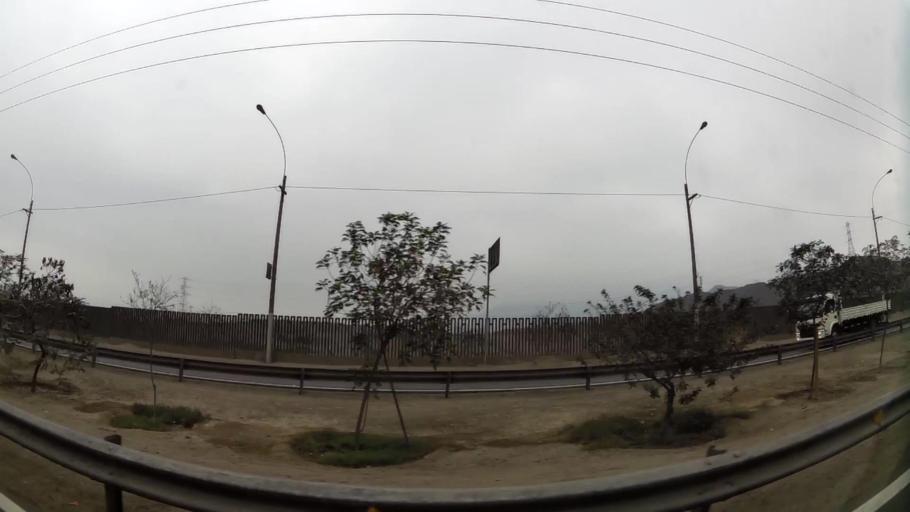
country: PE
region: Lima
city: Lima
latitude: -12.0308
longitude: -76.9841
